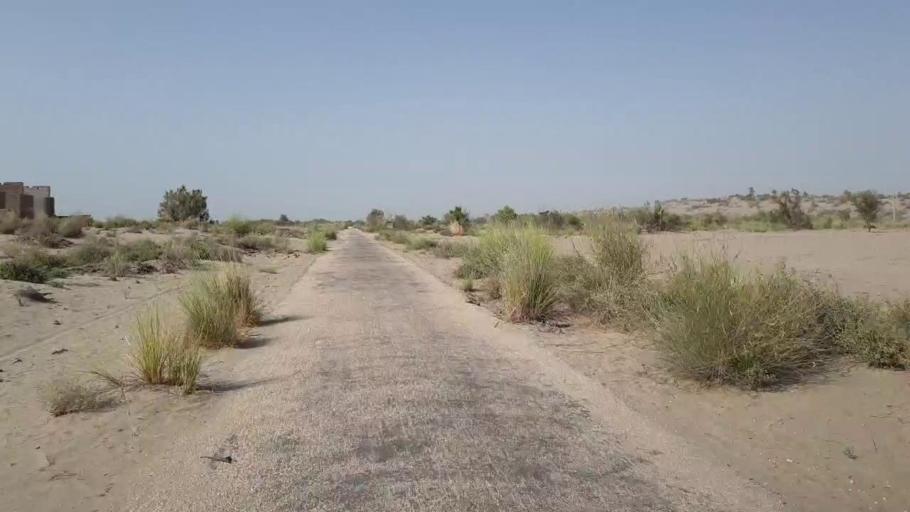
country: PK
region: Sindh
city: Jam Sahib
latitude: 26.5997
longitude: 68.9247
